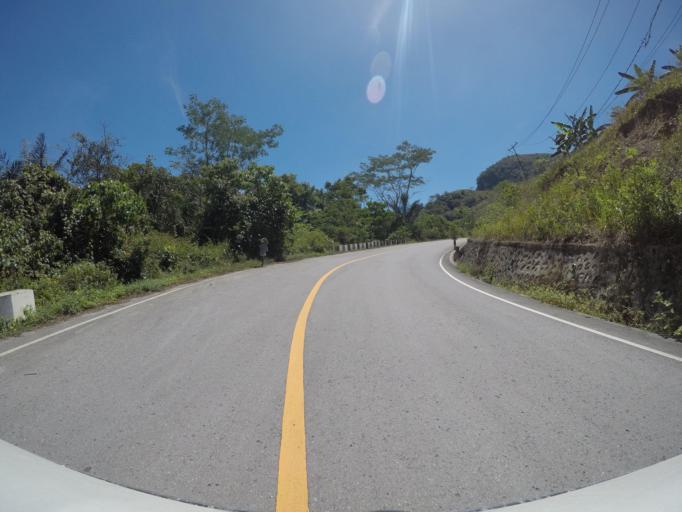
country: TL
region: Manatuto
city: Manatuto
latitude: -8.7698
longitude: 125.9653
